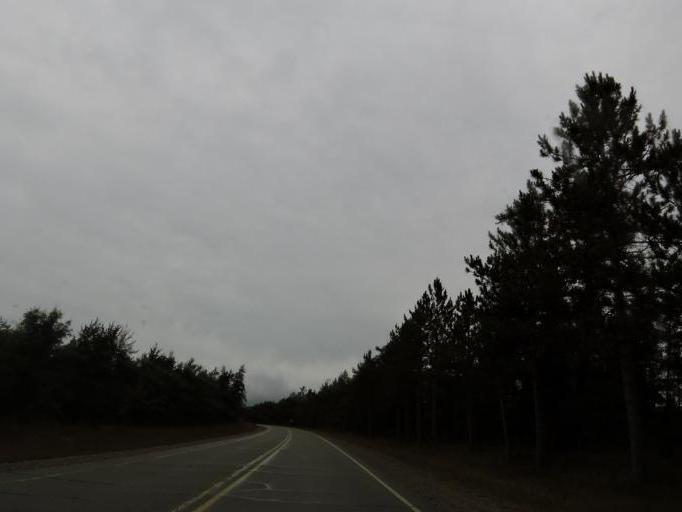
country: US
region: Michigan
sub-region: Roscommon County
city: Roscommon
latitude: 44.4600
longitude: -84.5281
